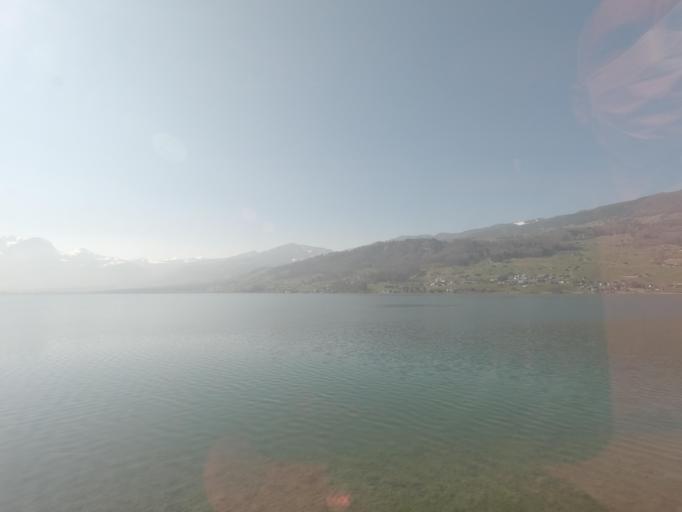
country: CH
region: Obwalden
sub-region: Obwalden
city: Sachseln
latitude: 46.8750
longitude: 8.2417
